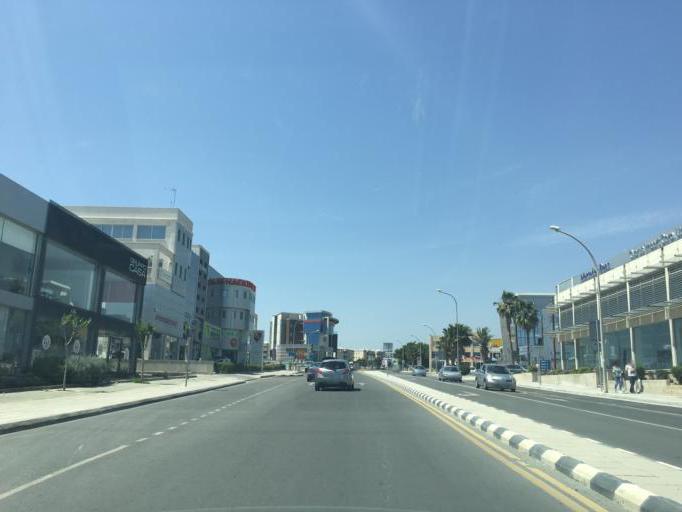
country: CY
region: Limassol
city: Limassol
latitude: 34.6986
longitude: 33.0627
